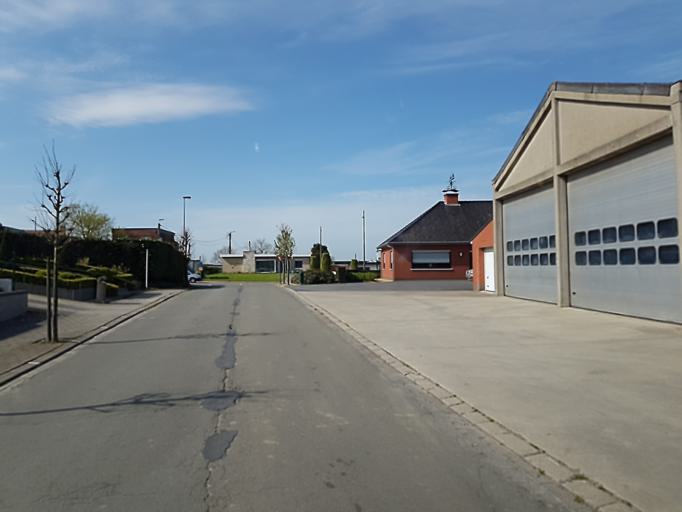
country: BE
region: Flanders
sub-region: Provincie West-Vlaanderen
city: Avelgem
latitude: 50.8204
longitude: 3.4280
